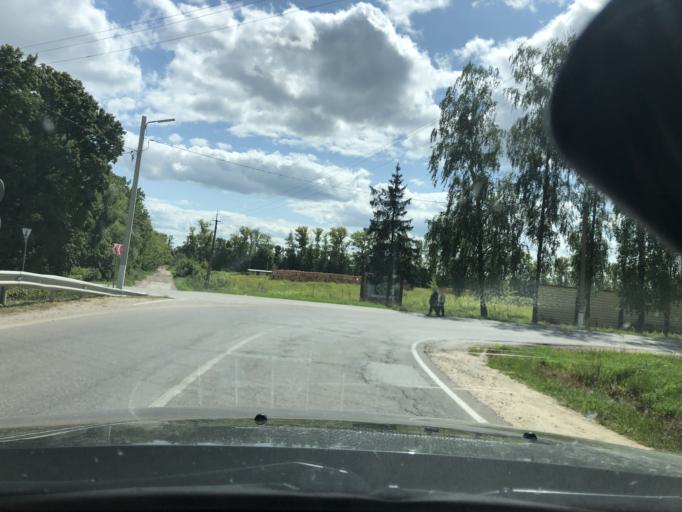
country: RU
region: Tula
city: Gorelki
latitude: 54.3367
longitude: 37.5631
